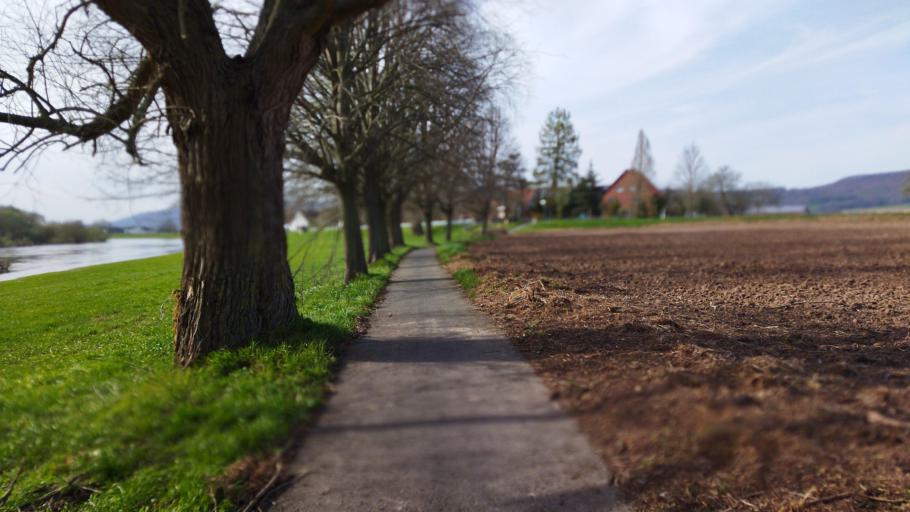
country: DE
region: Lower Saxony
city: Buchholz
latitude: 52.1836
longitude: 9.1543
